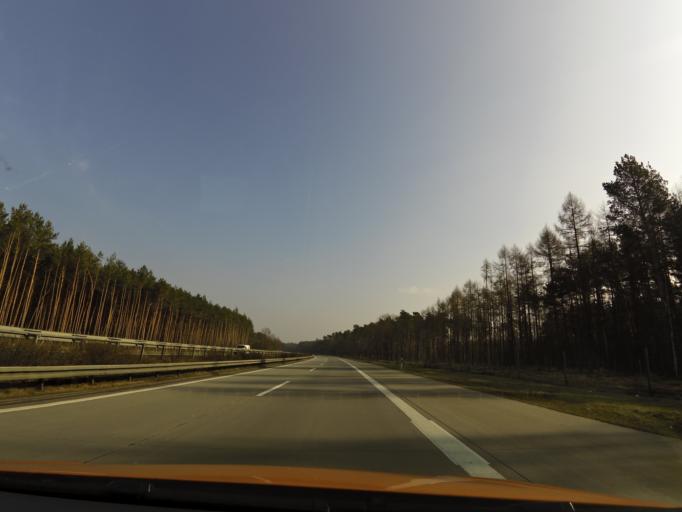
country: DE
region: Brandenburg
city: Berkenbruck
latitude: 52.3361
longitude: 14.1440
